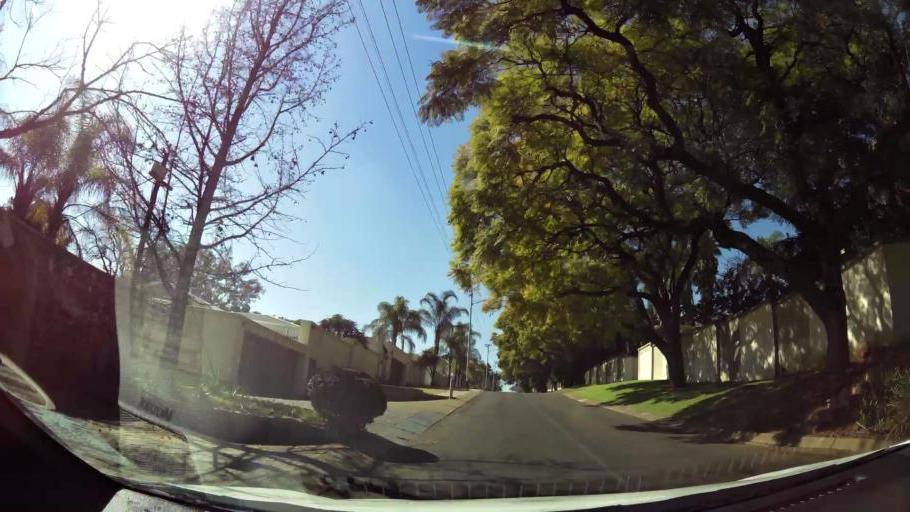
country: ZA
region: Gauteng
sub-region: City of Tshwane Metropolitan Municipality
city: Pretoria
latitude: -25.7821
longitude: 28.2318
